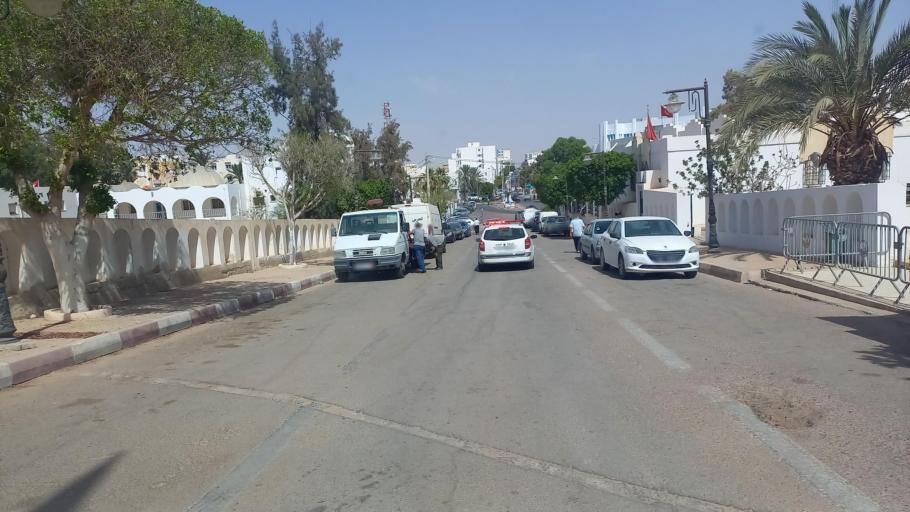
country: TN
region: Madanin
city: Medenine
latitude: 33.3421
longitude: 10.4922
